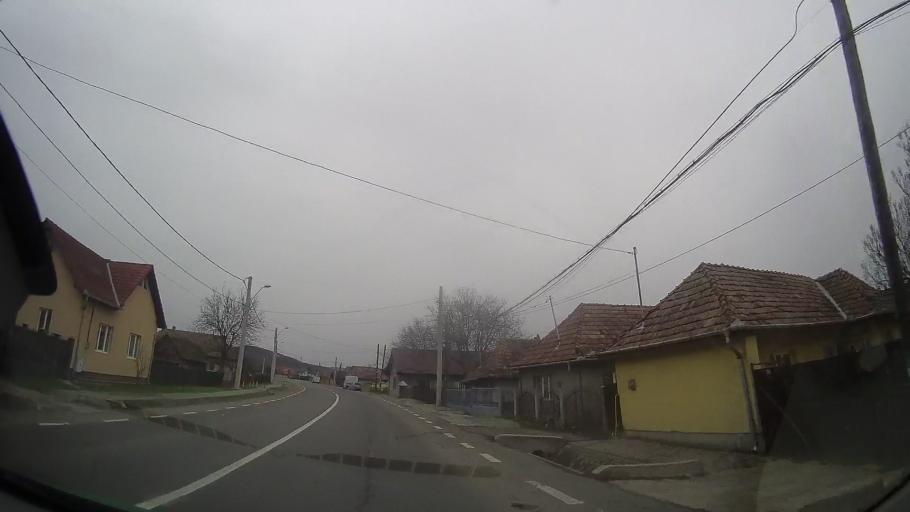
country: RO
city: Remetea
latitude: 46.5999
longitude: 24.5307
